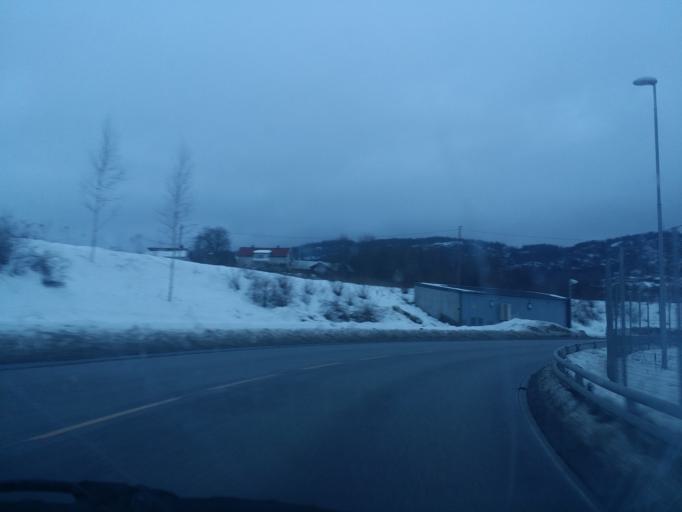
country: NO
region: Akershus
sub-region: Baerum
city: Skui
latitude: 59.9246
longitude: 10.4588
